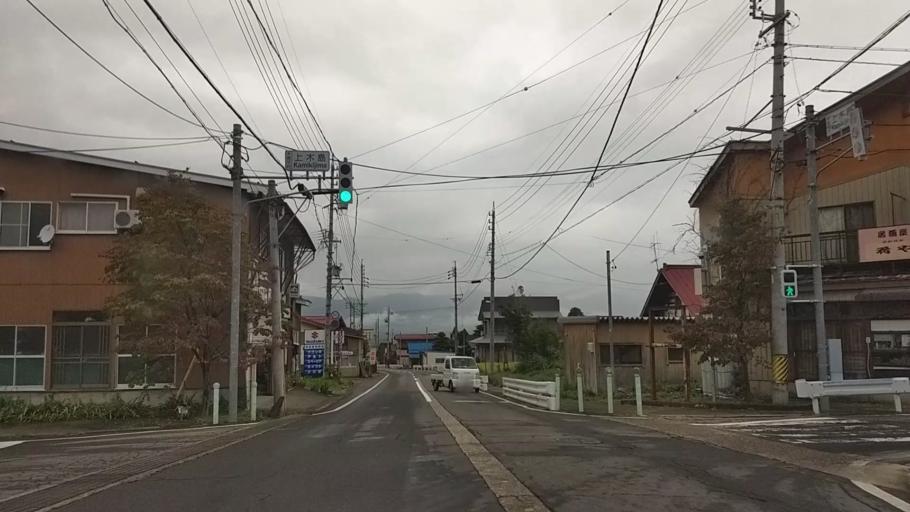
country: JP
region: Nagano
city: Iiyama
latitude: 36.8392
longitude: 138.4079
